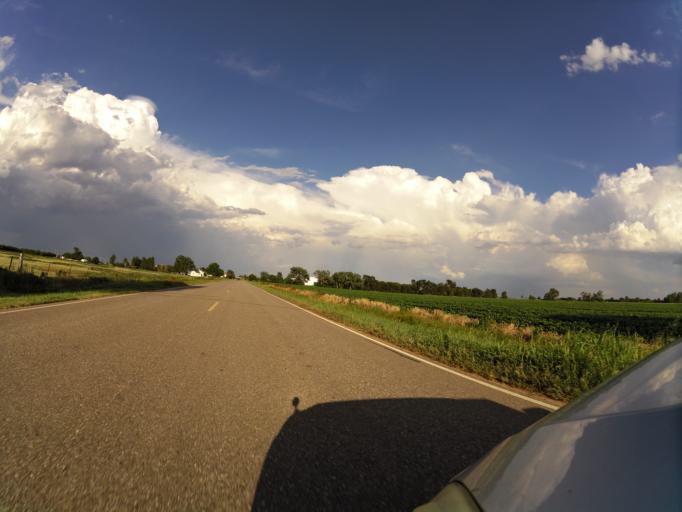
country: US
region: Kansas
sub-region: Reno County
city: South Hutchinson
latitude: 37.9410
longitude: -97.8927
